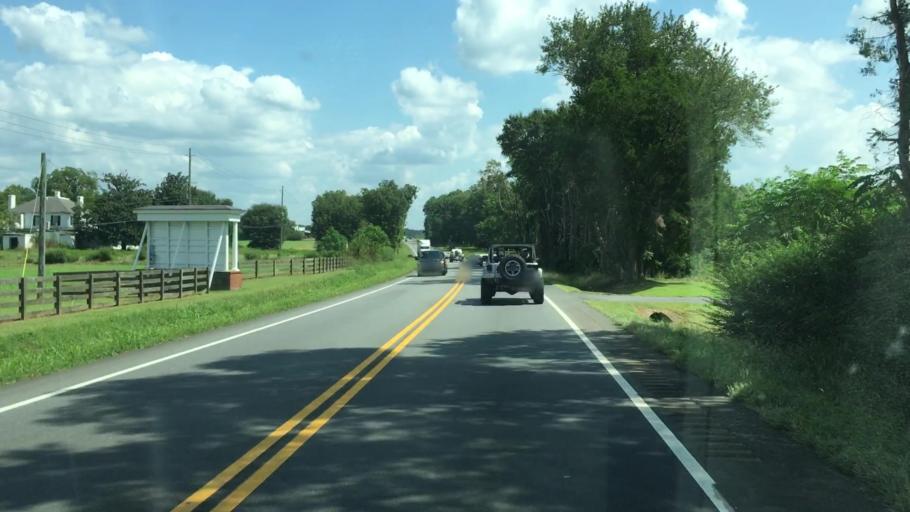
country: US
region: Georgia
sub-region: Morgan County
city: Madison
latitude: 33.5448
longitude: -83.4695
